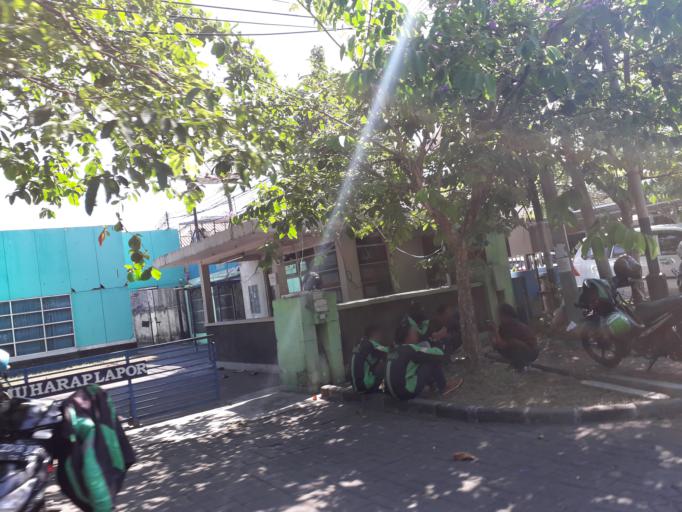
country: ID
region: Daerah Istimewa Yogyakarta
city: Yogyakarta
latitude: -7.7715
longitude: 110.3754
